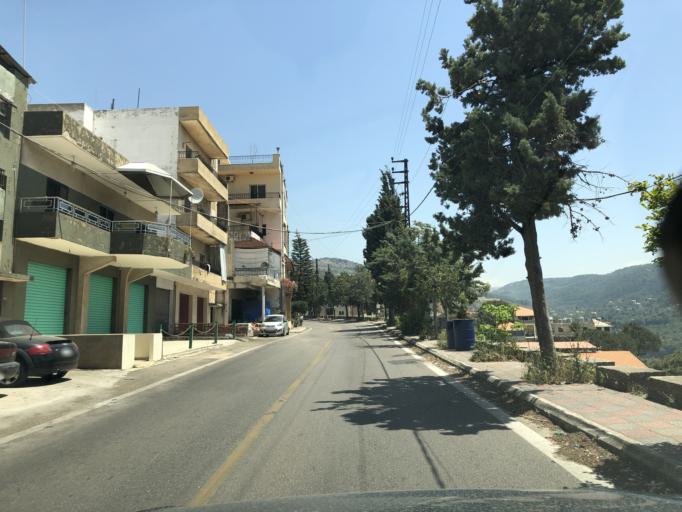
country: LB
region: Mont-Liban
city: Beit ed Dine
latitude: 33.6876
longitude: 35.5248
